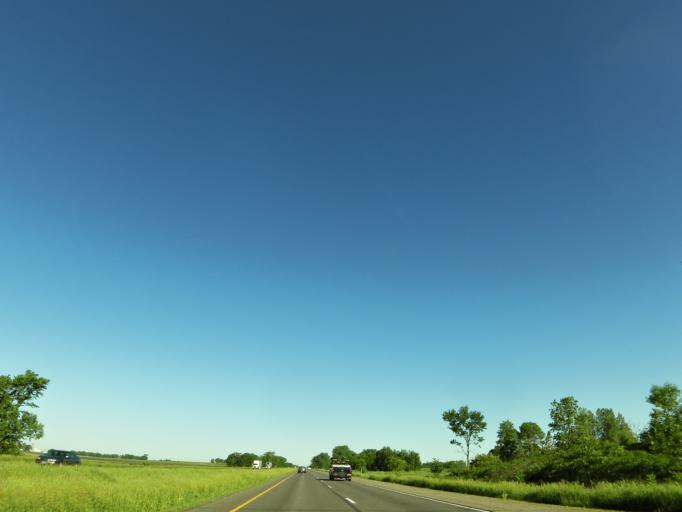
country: US
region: Minnesota
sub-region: Stearns County
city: Albany
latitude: 45.6346
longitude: -94.6068
